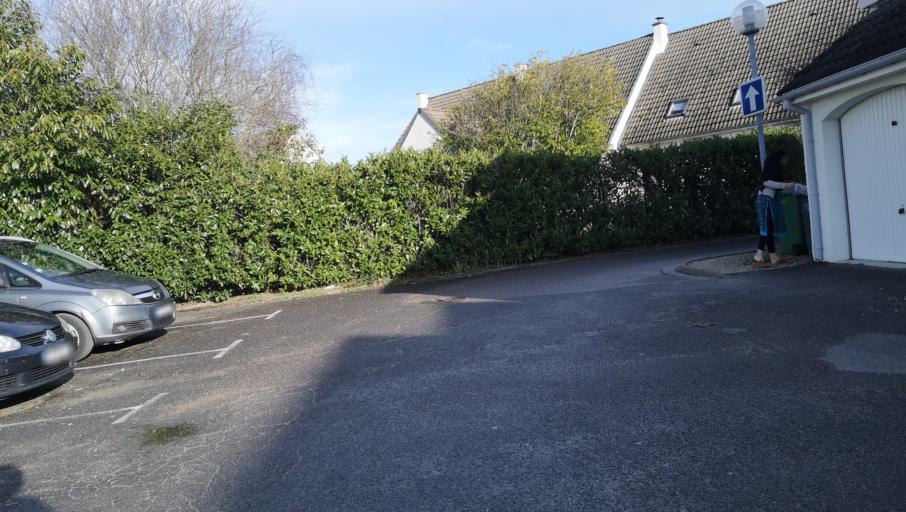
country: FR
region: Centre
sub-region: Departement du Loiret
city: Saint-Pryve-Saint-Mesmin
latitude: 47.8759
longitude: 1.8695
